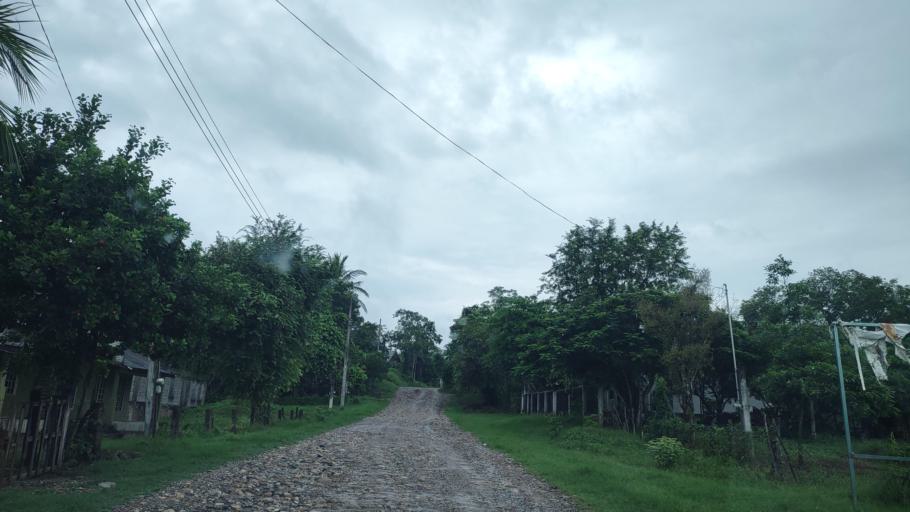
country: MX
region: San Luis Potosi
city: Tanquian de Escobedo
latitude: 21.5421
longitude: -98.5511
